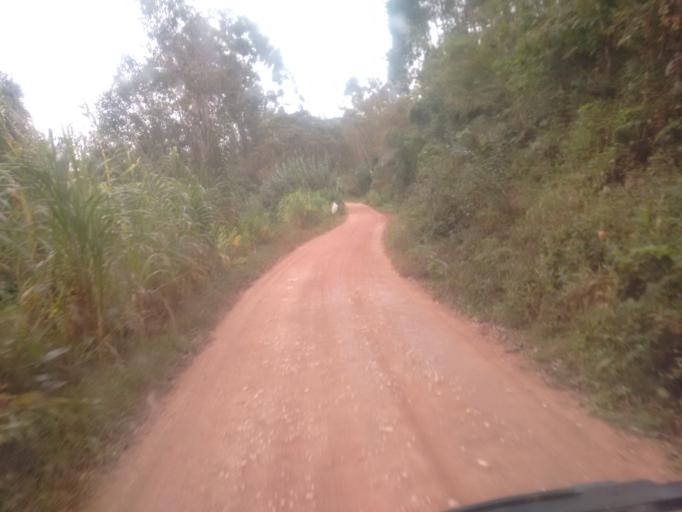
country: BR
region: Rio Grande do Sul
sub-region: Camaqua
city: Camaqua
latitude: -30.7220
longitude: -51.8715
